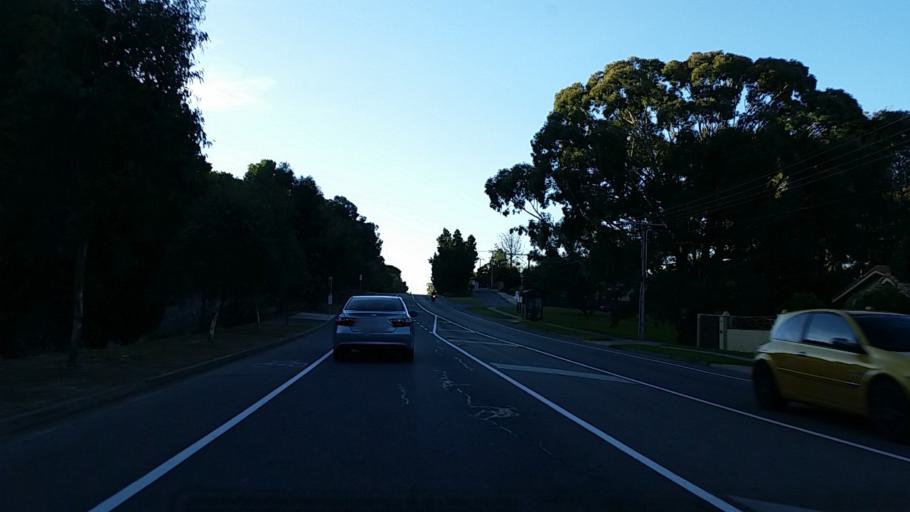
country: AU
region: South Australia
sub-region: Campbelltown
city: Athelstone
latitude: -34.8538
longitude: 138.6944
